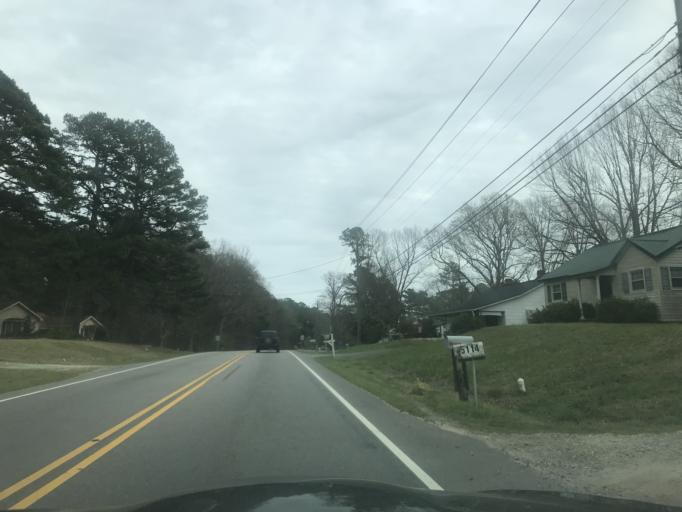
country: US
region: North Carolina
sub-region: Franklin County
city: Franklinton
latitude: 36.1021
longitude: -78.4316
